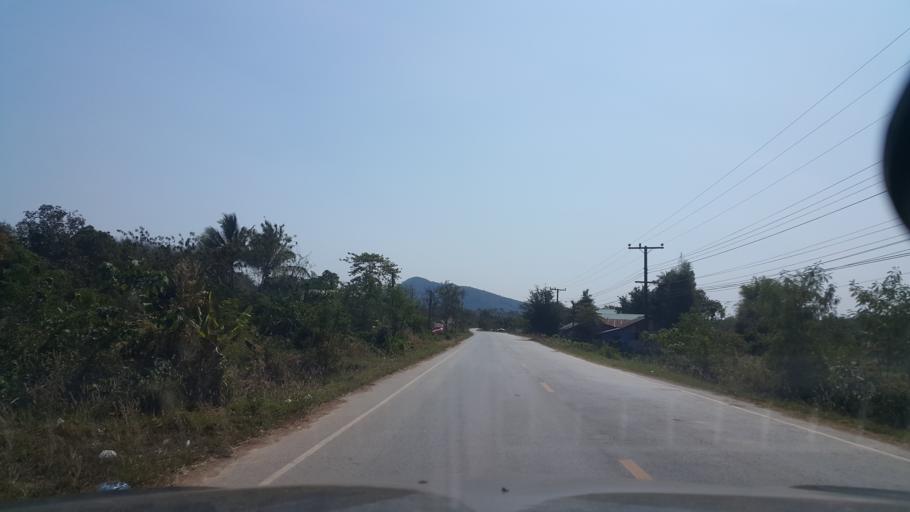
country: TH
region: Changwat Udon Thani
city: Na Yung
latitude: 17.8839
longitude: 102.0839
